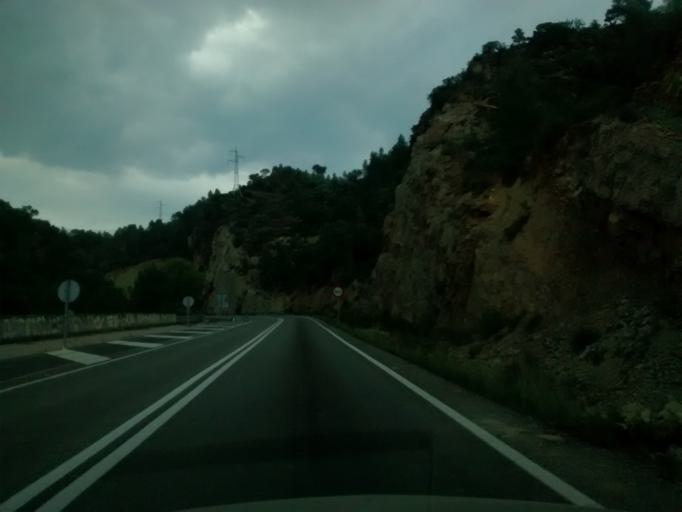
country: ES
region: Catalonia
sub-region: Provincia de Tarragona
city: Benifallet
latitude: 40.9820
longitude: 0.5161
